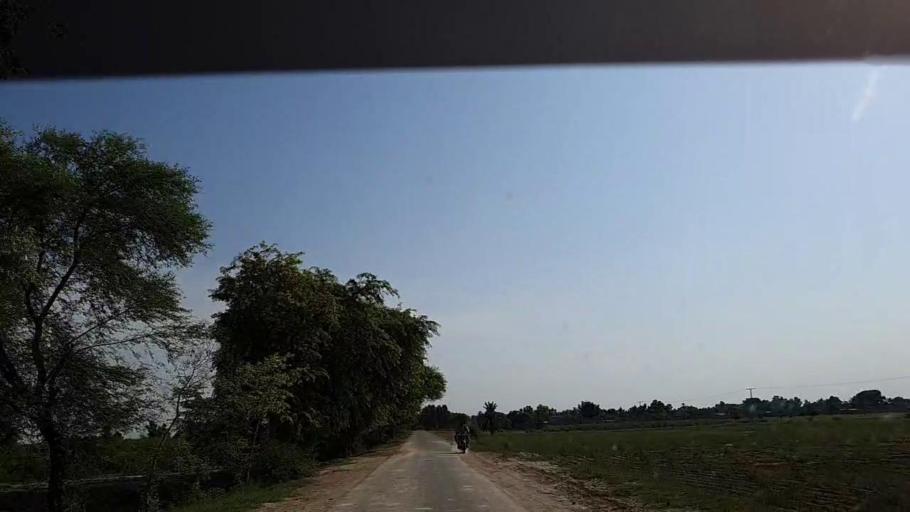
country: PK
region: Sindh
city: Adilpur
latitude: 27.9254
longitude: 69.2500
